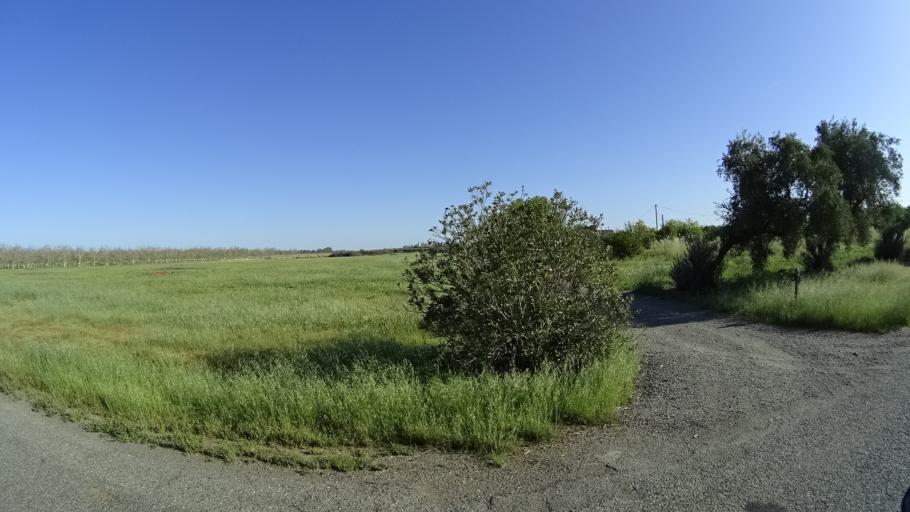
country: US
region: California
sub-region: Glenn County
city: Orland
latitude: 39.6820
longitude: -122.1674
